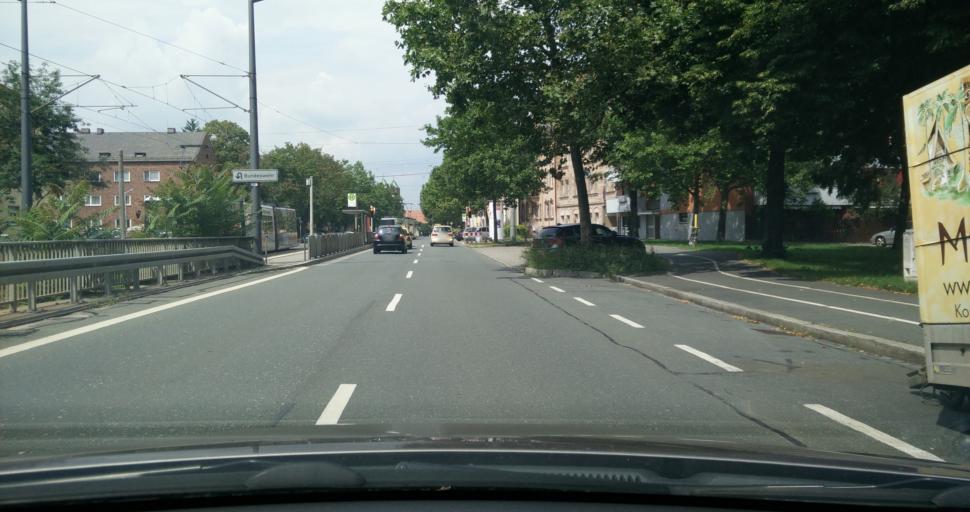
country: DE
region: Bavaria
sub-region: Regierungsbezirk Mittelfranken
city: Nuernberg
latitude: 49.4335
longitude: 11.0953
